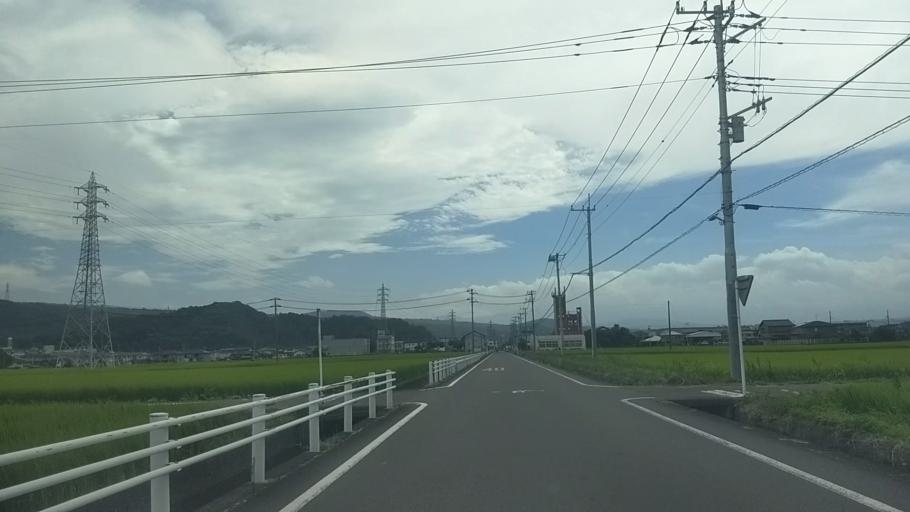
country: JP
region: Shizuoka
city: Mishima
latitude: 35.0614
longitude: 138.9475
